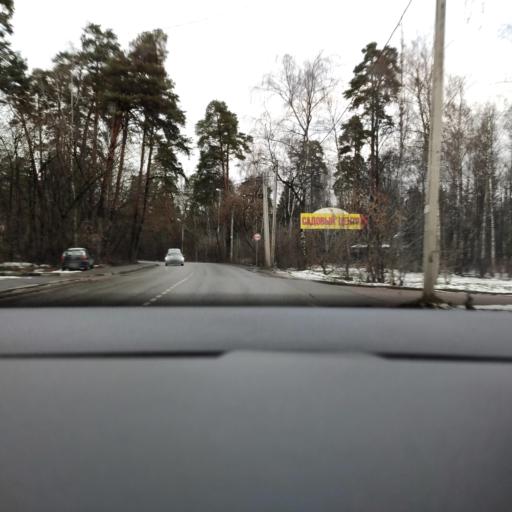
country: RU
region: Moskovskaya
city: Lesnyye Polyany
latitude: 55.9500
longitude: 37.8690
